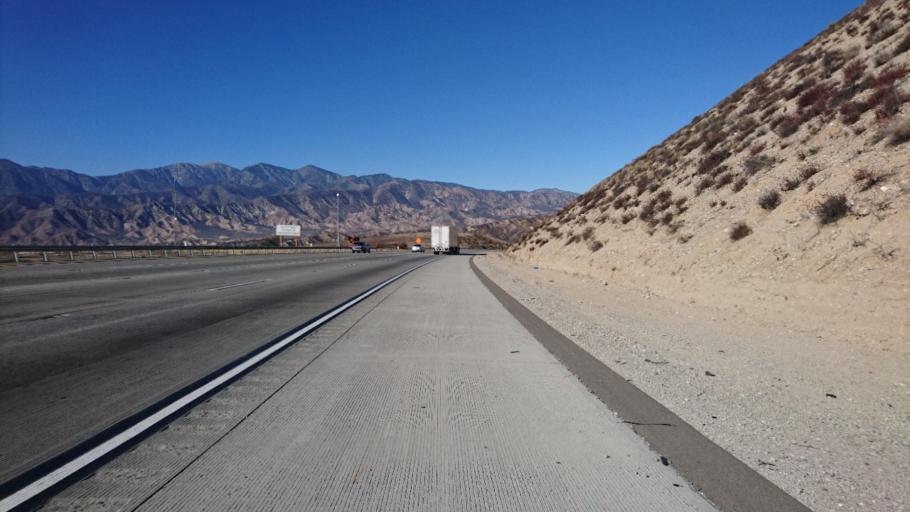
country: US
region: California
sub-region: San Bernardino County
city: Oak Hills
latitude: 34.3442
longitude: -117.4598
